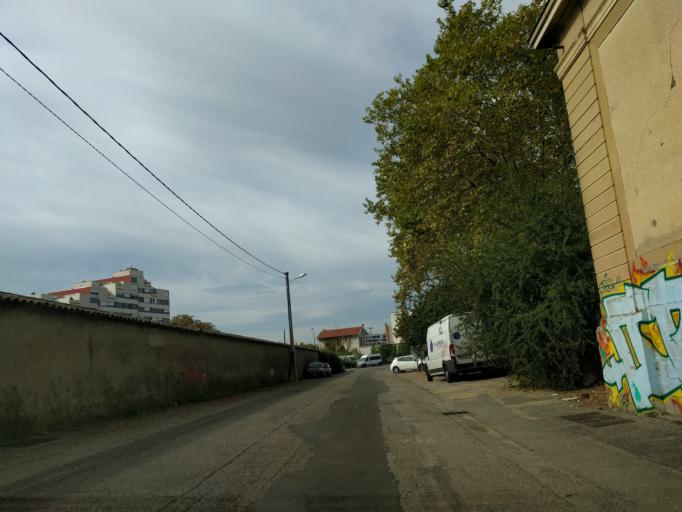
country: FR
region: Rhone-Alpes
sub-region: Departement du Rhone
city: Vaulx-en-Velin
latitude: 45.7664
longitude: 4.9117
